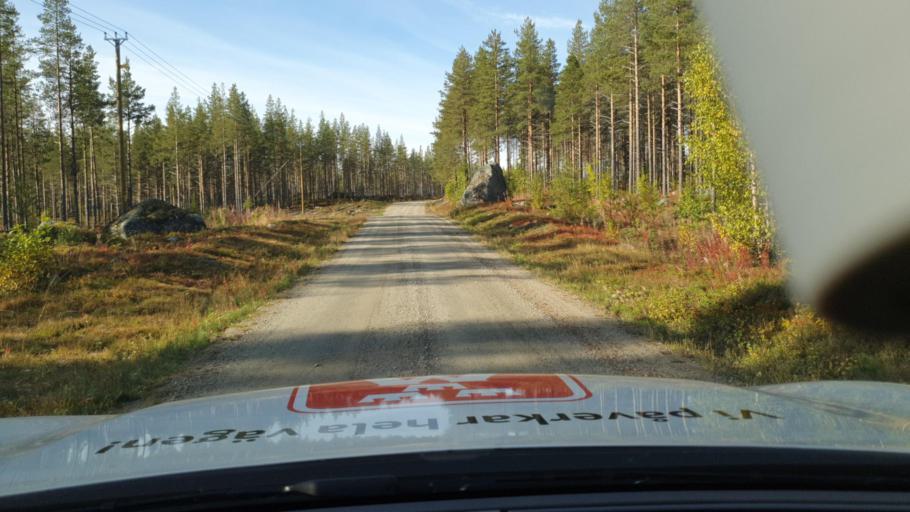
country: SE
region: Vaesterbotten
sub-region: Asele Kommun
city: Asele
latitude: 63.9899
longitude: 17.8387
